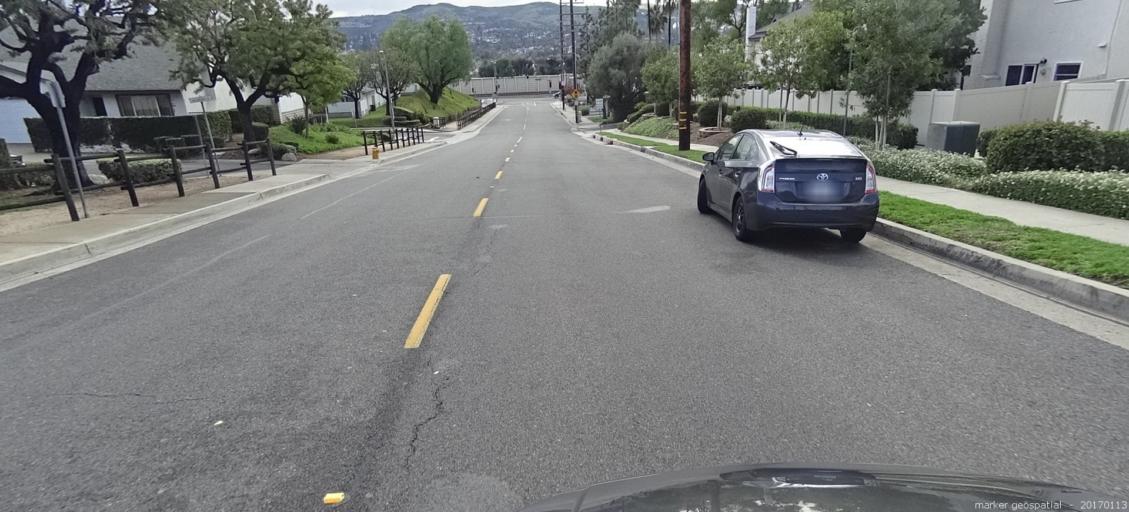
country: US
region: California
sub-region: Orange County
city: Yorba Linda
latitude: 33.8647
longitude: -117.7864
